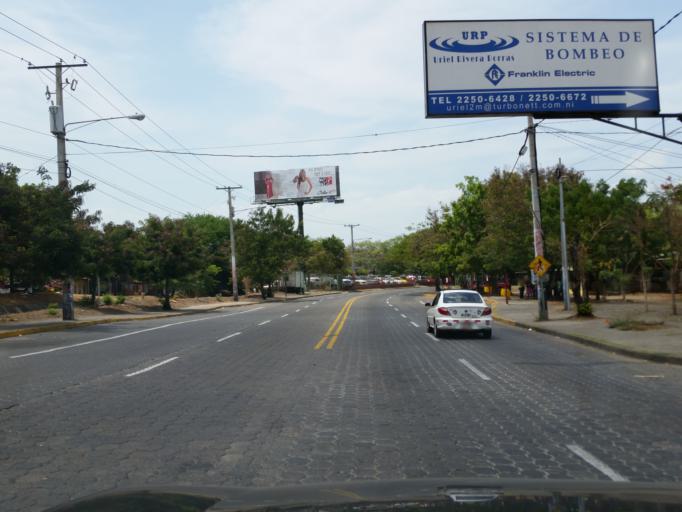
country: NI
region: Managua
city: Managua
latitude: 12.1475
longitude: -86.2412
